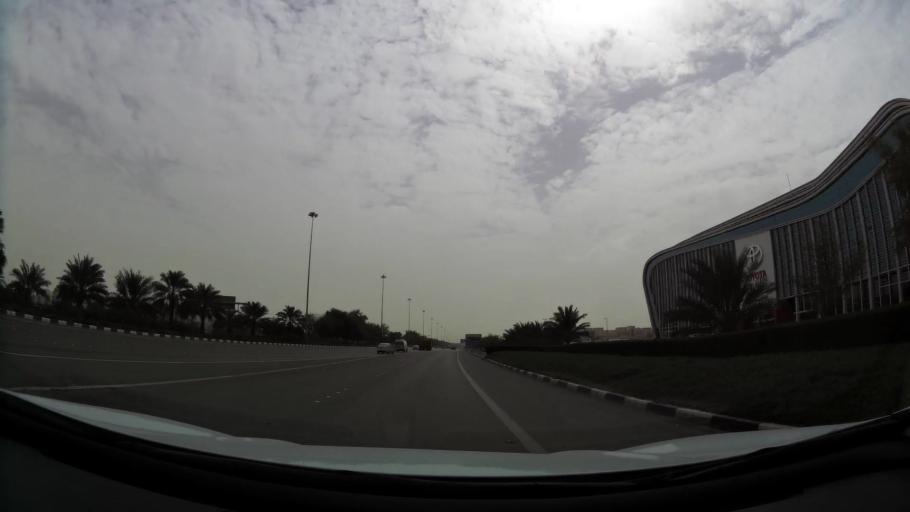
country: AE
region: Abu Dhabi
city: Abu Dhabi
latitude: 24.3420
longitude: 54.5261
